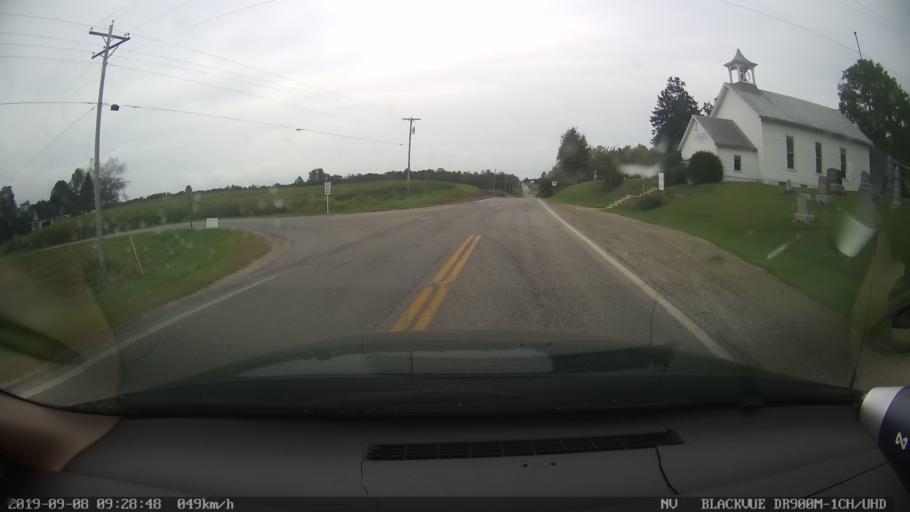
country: US
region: Ohio
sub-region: Morrow County
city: Mount Gilead
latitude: 40.5944
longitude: -82.7671
